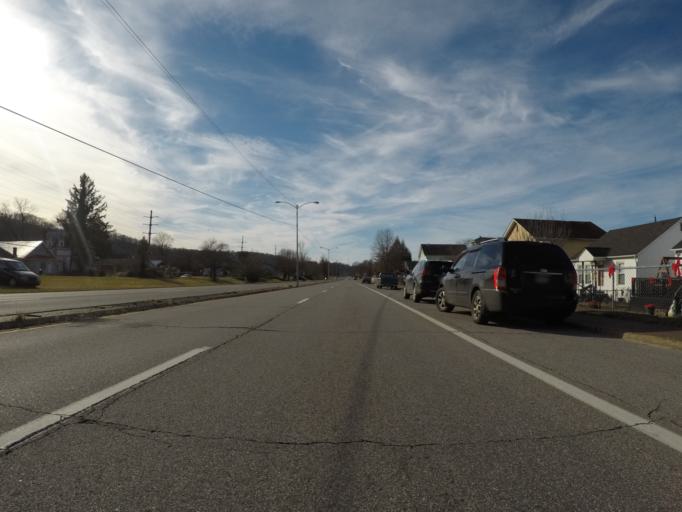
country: US
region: Ohio
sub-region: Lawrence County
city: Burlington
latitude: 38.4030
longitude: -82.5044
